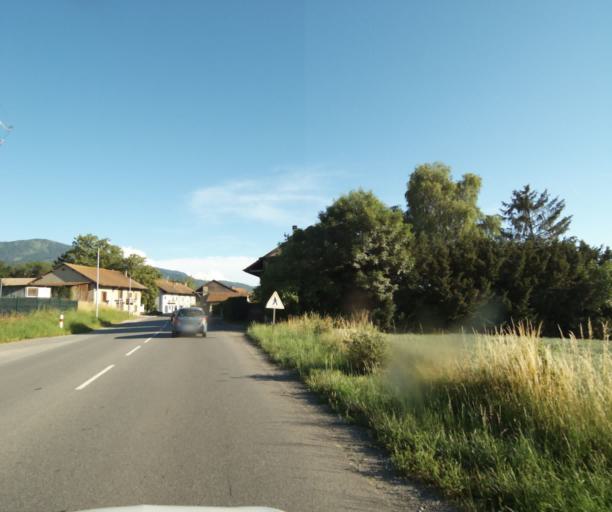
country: FR
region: Rhone-Alpes
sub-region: Departement de la Haute-Savoie
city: Loisin
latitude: 46.2734
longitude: 6.3128
